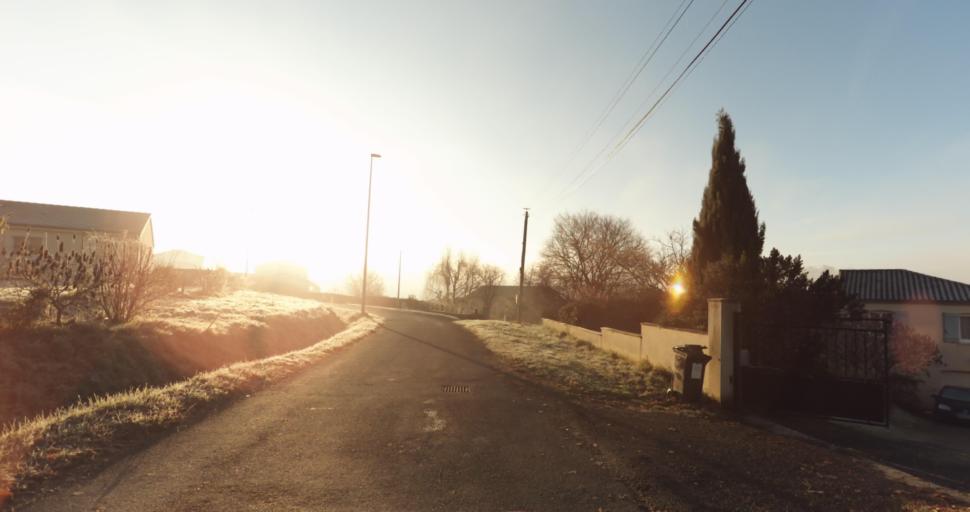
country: FR
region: Limousin
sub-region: Departement de la Haute-Vienne
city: Aixe-sur-Vienne
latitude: 45.7930
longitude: 1.1579
